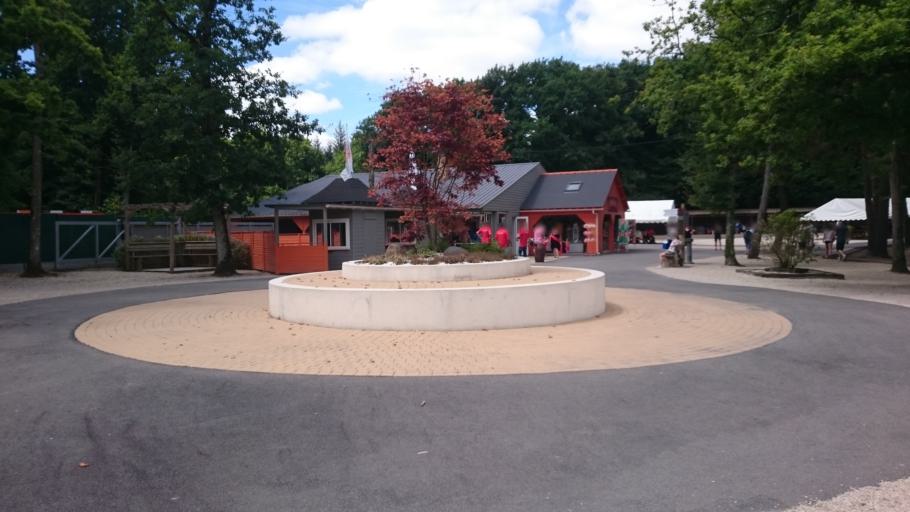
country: FR
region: Brittany
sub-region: Departement d'Ille-et-Vilaine
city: Meillac
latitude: 48.4386
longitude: -1.8316
